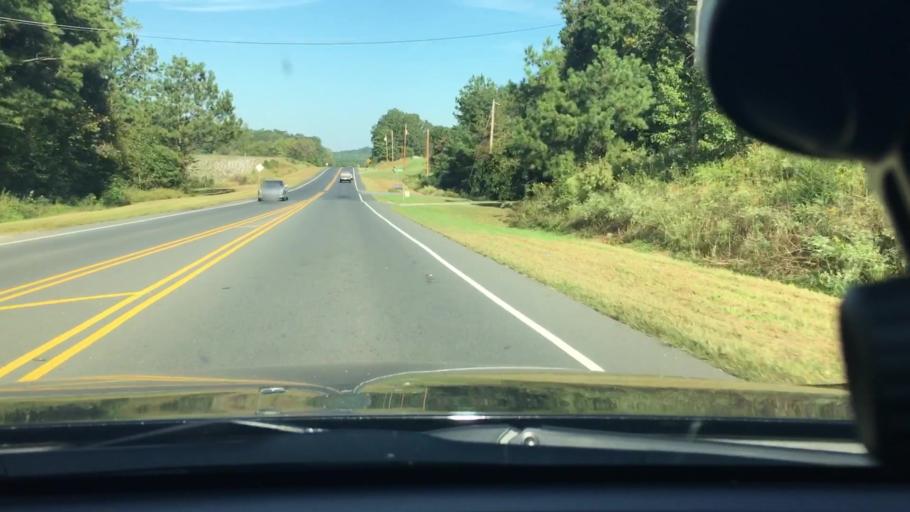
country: US
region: North Carolina
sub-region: Stanly County
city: Albemarle
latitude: 35.3785
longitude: -80.1718
